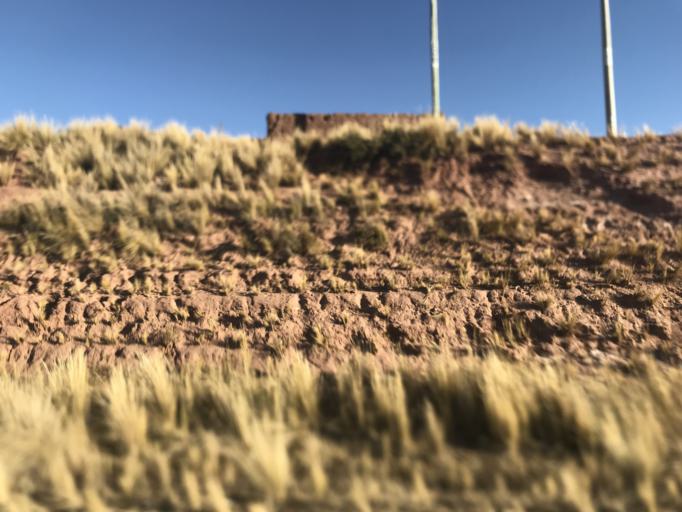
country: BO
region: La Paz
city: Tiahuanaco
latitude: -16.5631
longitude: -68.6261
